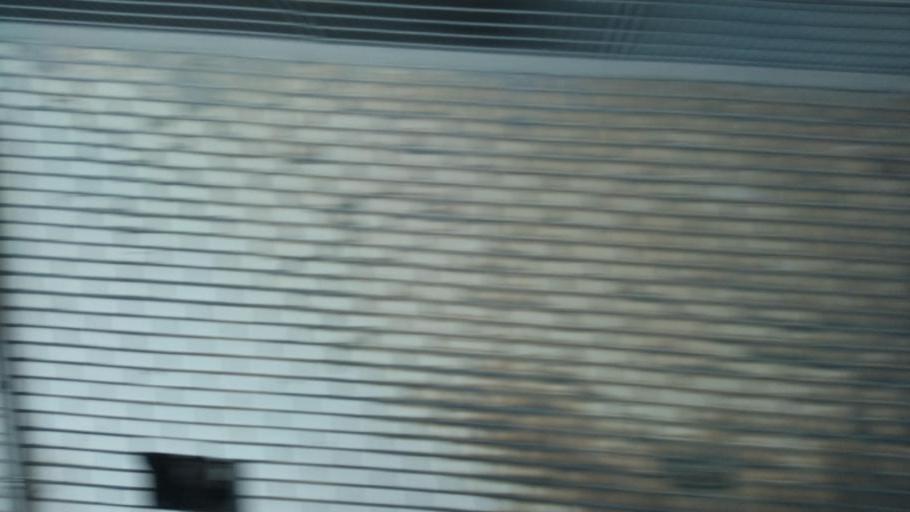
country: TW
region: Taiwan
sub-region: Hualien
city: Hualian
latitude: 24.2215
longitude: 121.6957
